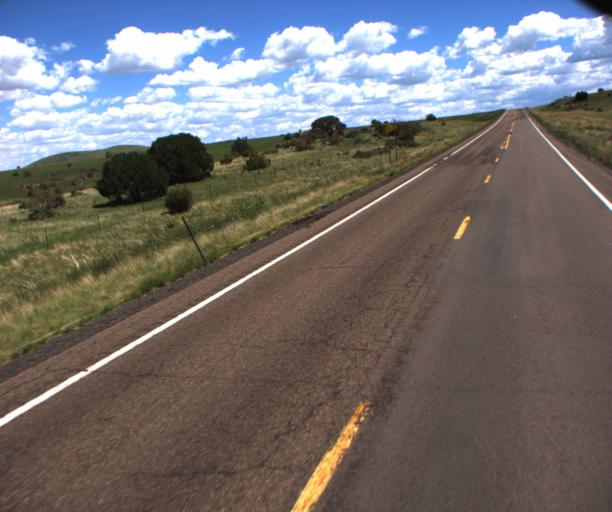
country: US
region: Arizona
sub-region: Apache County
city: Springerville
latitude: 34.2289
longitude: -109.4921
